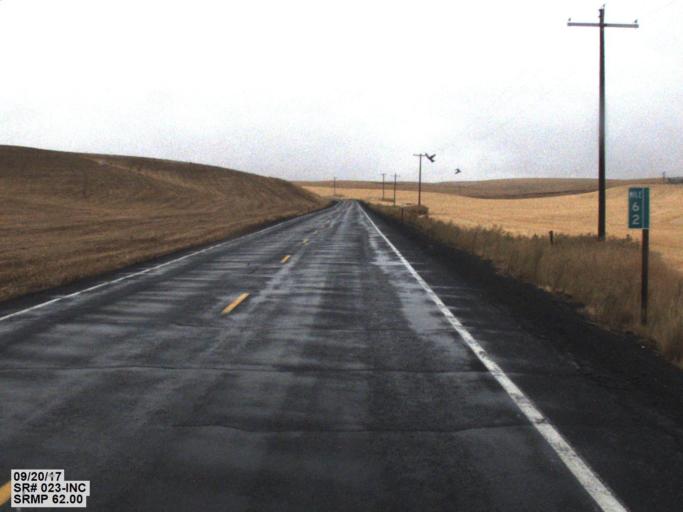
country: US
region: Washington
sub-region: Lincoln County
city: Davenport
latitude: 47.4709
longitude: -118.1855
